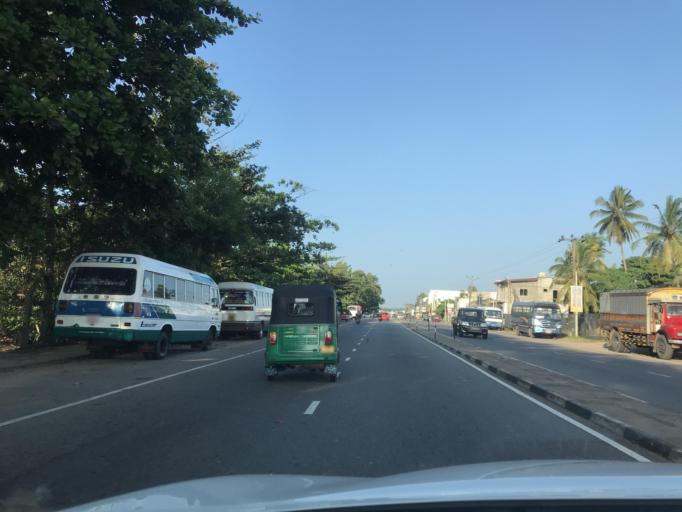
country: LK
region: Western
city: Ja Ela
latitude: 7.0954
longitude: 79.9054
